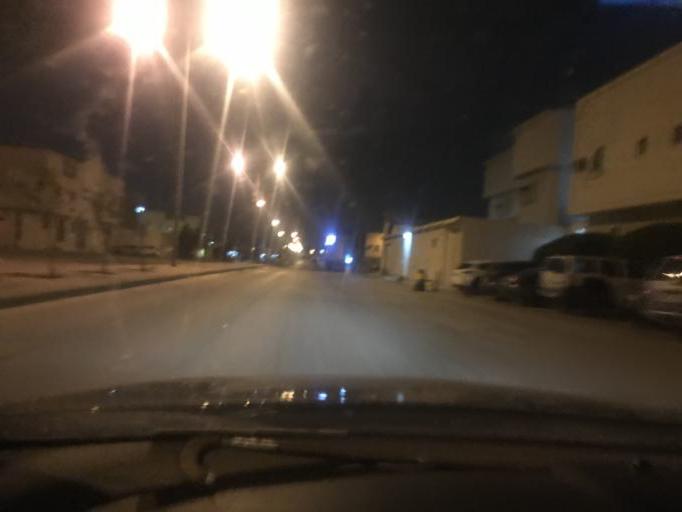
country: SA
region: Ar Riyad
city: Riyadh
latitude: 24.7492
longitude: 46.7479
